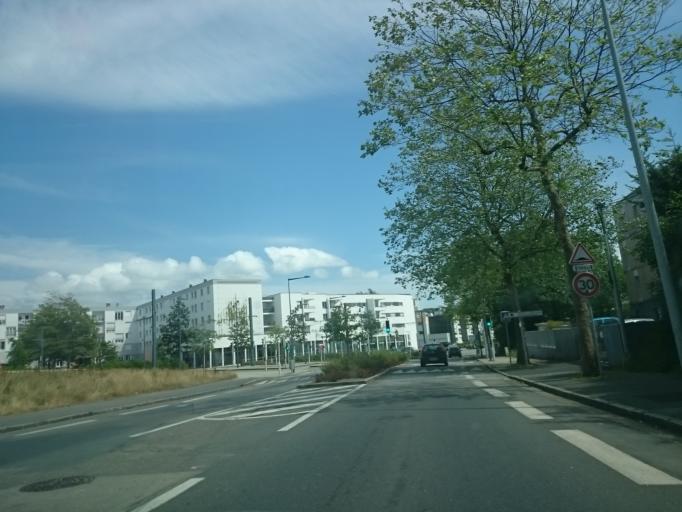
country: FR
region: Brittany
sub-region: Departement du Finistere
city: Brest
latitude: 48.4111
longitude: -4.4721
